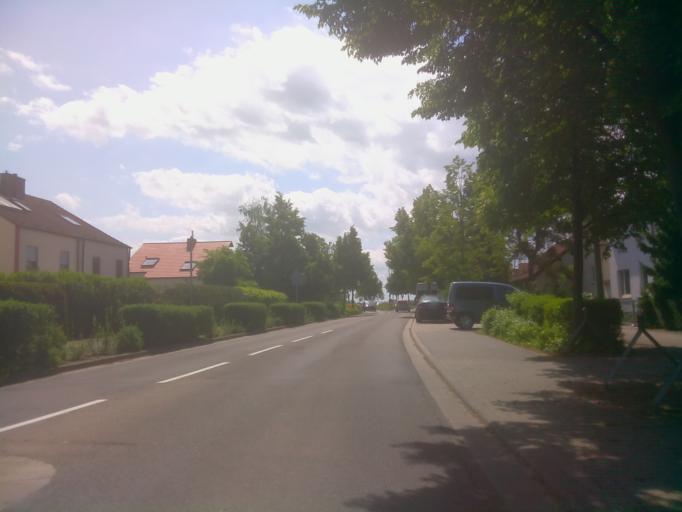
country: DE
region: Rheinland-Pfalz
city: Neuhofen
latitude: 49.4174
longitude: 8.4305
